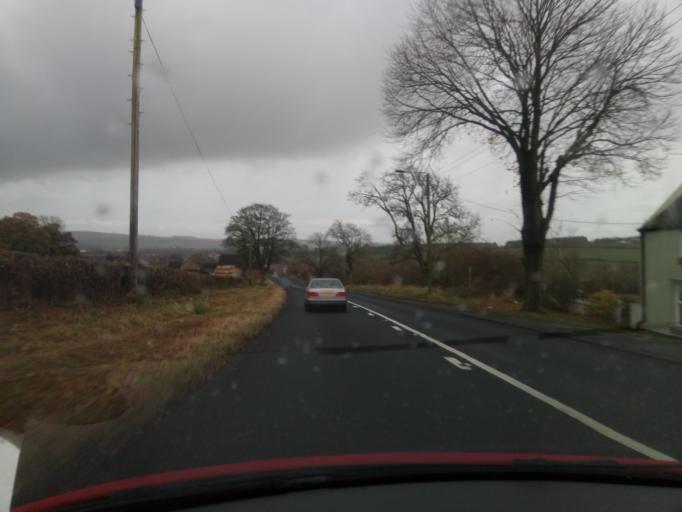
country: GB
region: England
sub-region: County Durham
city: High Etherley
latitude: 54.6390
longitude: -1.7429
